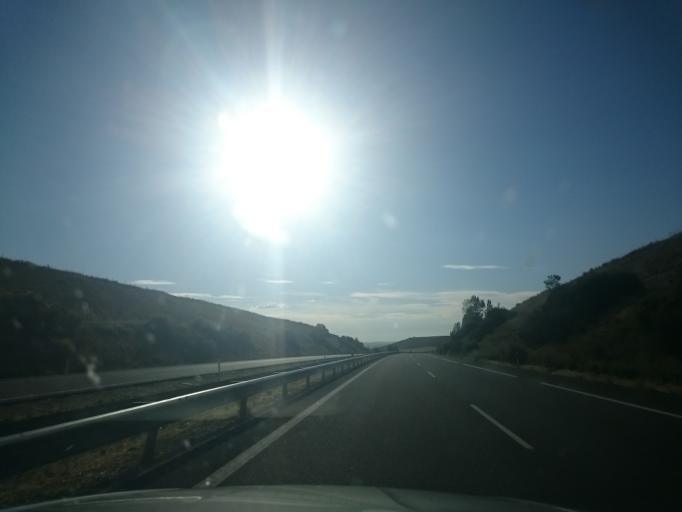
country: ES
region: Castille and Leon
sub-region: Provincia de Burgos
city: Pedrosa del Paramo
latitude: 42.3900
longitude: -3.9903
